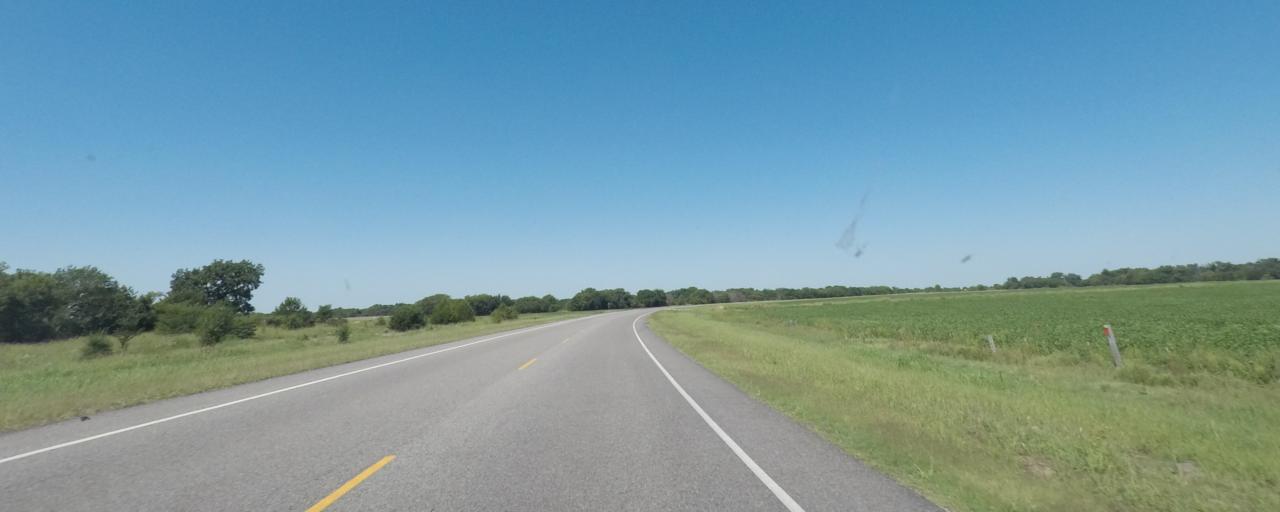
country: US
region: Oklahoma
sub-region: Kay County
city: Blackwell
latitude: 36.9425
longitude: -97.3526
